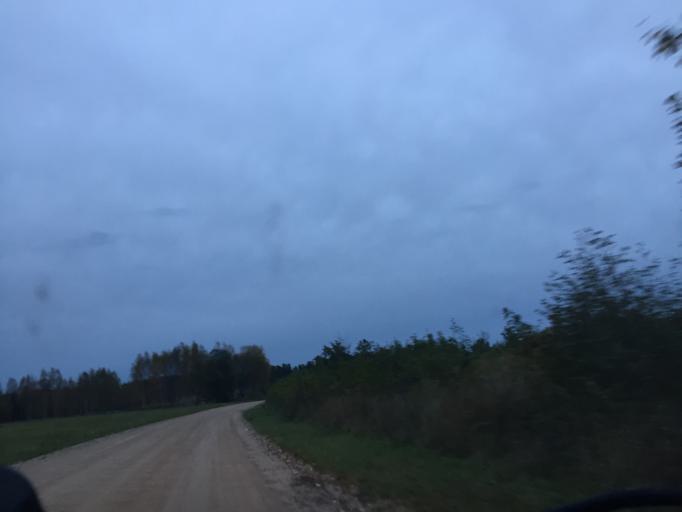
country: LV
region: Adazi
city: Adazi
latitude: 57.0841
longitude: 24.3541
